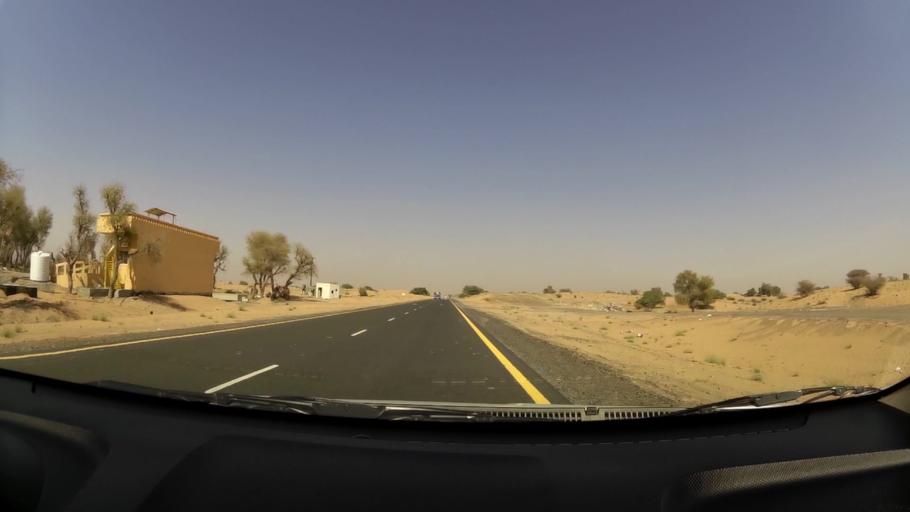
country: AE
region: Umm al Qaywayn
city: Umm al Qaywayn
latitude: 25.4795
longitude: 55.6229
